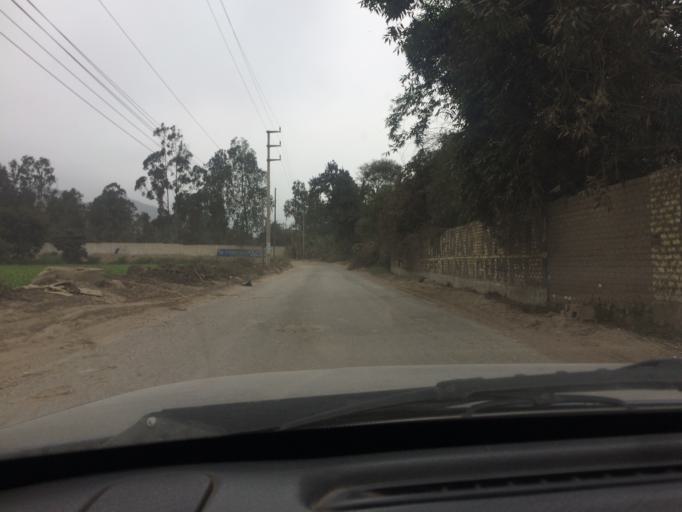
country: PE
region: Lima
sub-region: Lima
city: Cieneguilla
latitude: -12.1786
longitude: -76.8637
